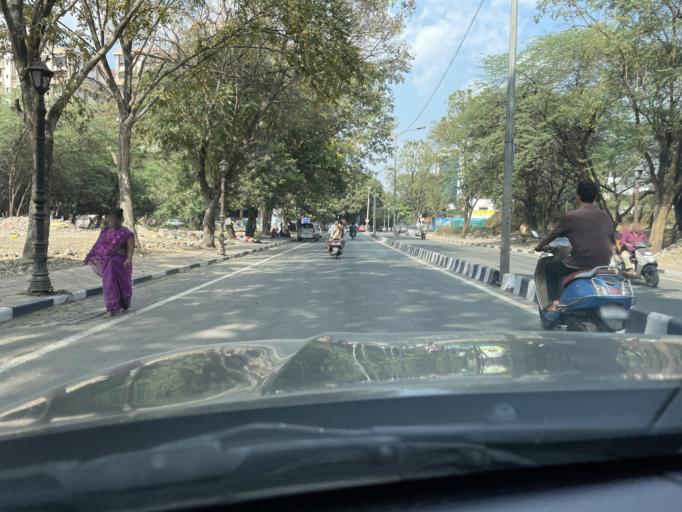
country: IN
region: Maharashtra
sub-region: Pune Division
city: Pune
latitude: 18.4886
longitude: 73.9000
